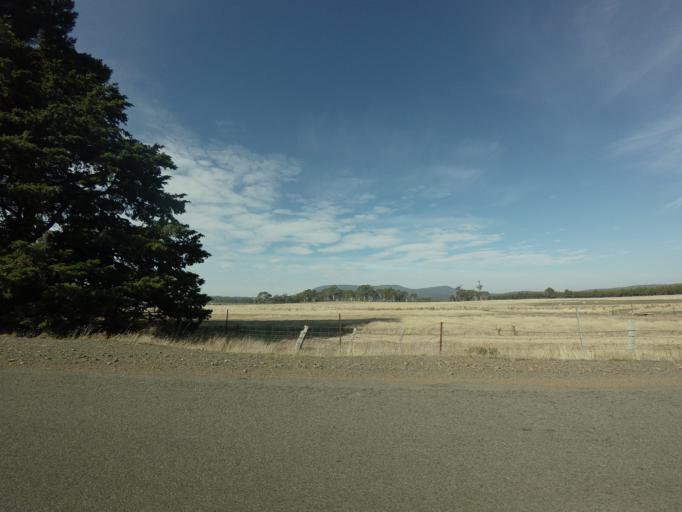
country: AU
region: Tasmania
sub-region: Sorell
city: Sorell
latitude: -42.4399
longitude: 147.4723
